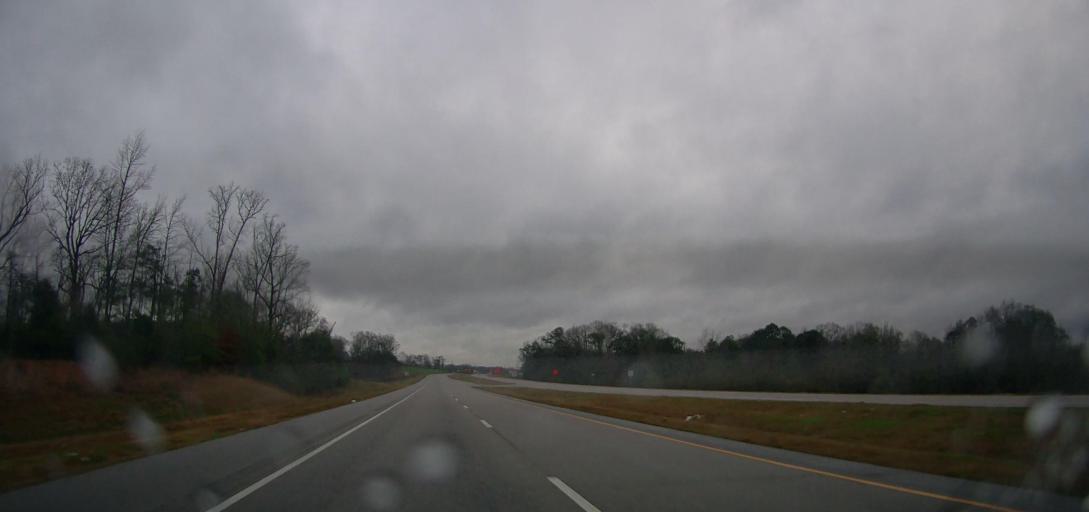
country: US
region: Alabama
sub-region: Bibb County
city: Centreville
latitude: 32.9408
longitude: -87.0731
